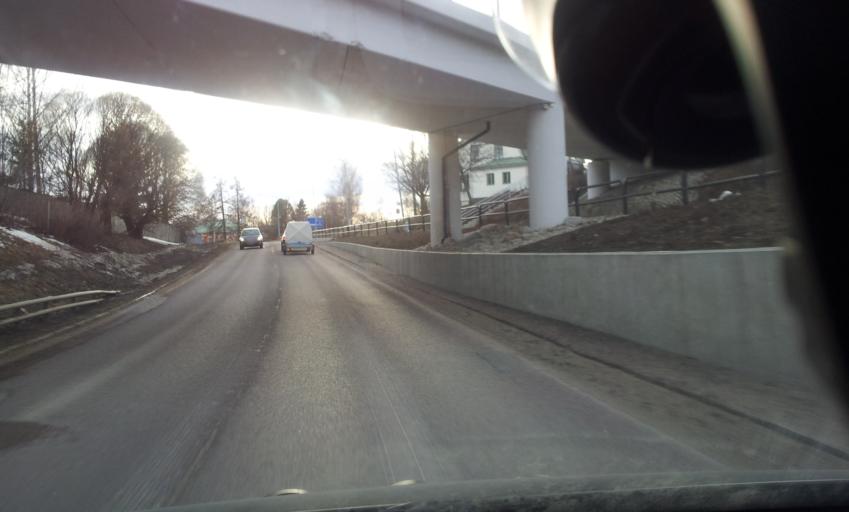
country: SE
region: Gaevleborg
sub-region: Ljusdals Kommun
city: Ljusdal
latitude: 61.8300
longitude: 16.0857
